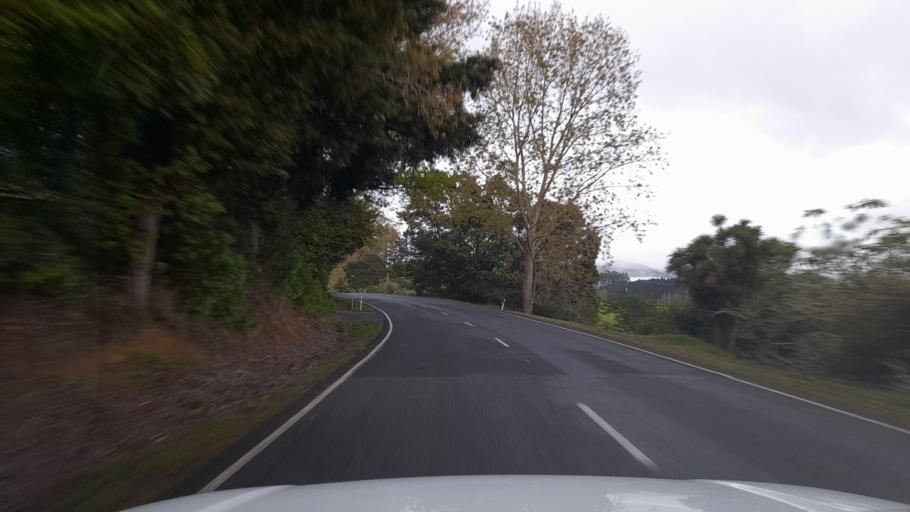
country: NZ
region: Northland
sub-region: Whangarei
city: Maungatapere
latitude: -35.7065
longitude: 174.0200
